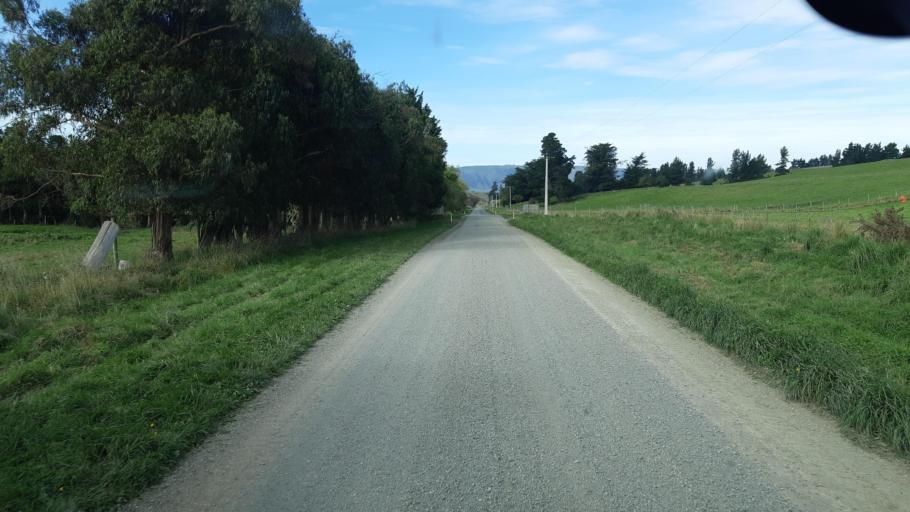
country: NZ
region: Canterbury
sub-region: Timaru District
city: Pleasant Point
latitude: -44.2108
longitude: 170.8064
